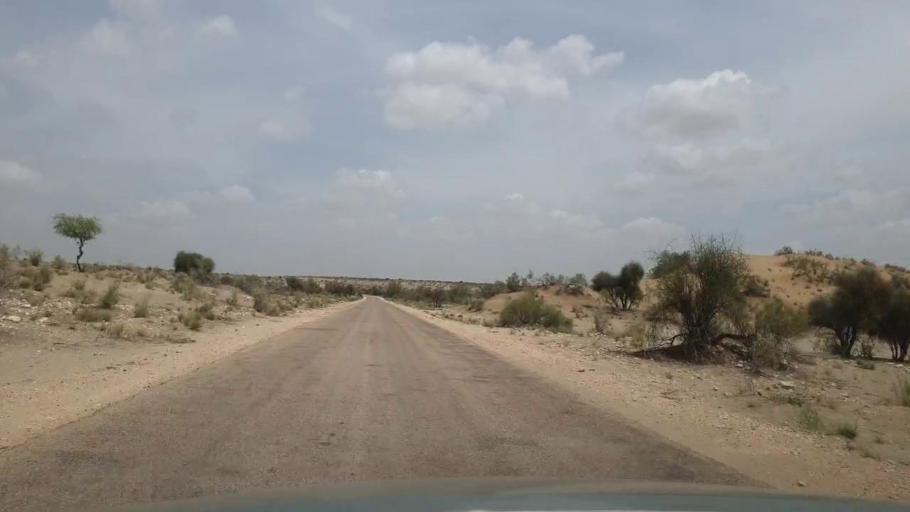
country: PK
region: Sindh
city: Kot Diji
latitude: 27.1737
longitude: 69.1936
